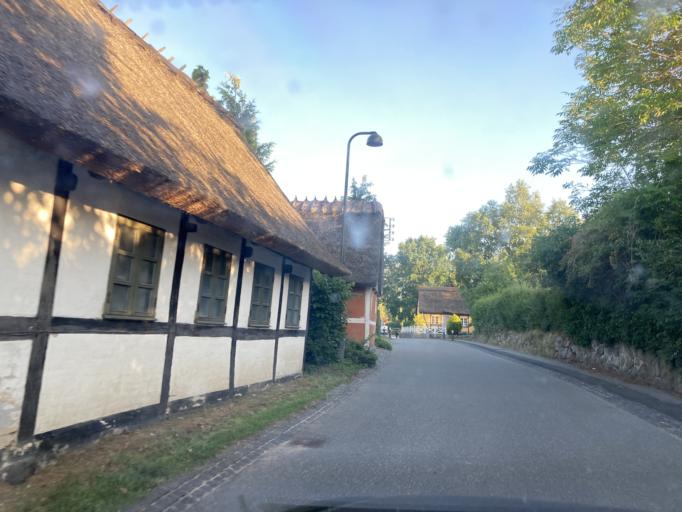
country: DK
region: Zealand
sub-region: Lejre Kommune
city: Lejre
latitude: 55.6461
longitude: 11.9608
